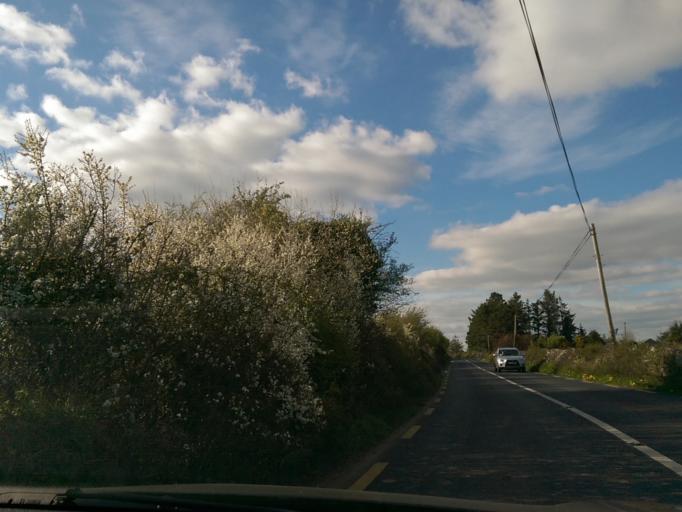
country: IE
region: Connaught
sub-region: County Galway
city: Portumna
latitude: 53.1189
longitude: -8.2398
